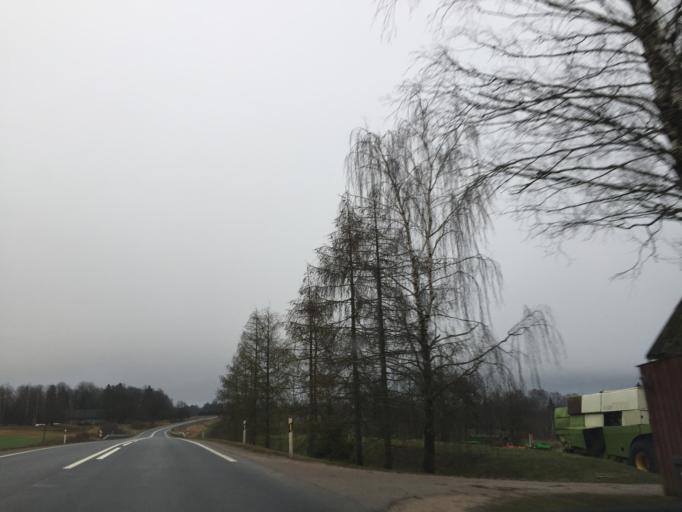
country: LV
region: Aizpute
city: Aizpute
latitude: 56.5892
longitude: 21.6084
